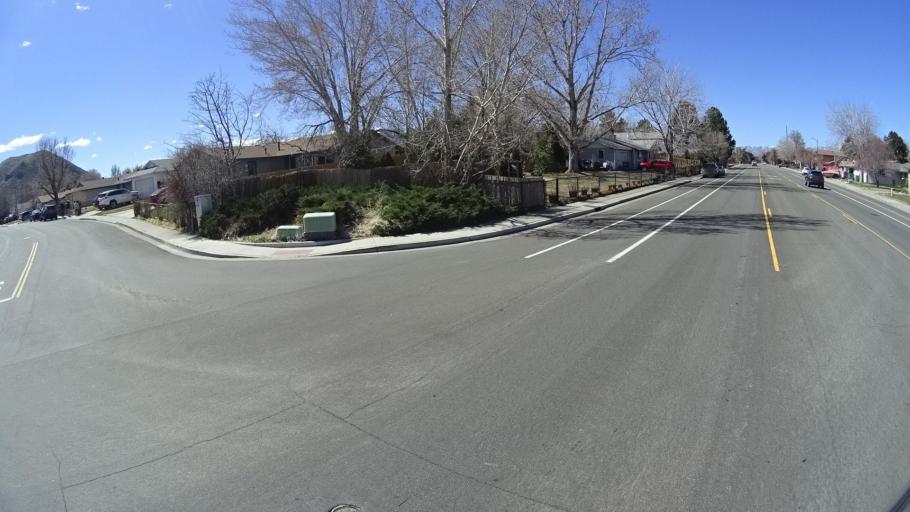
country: US
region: Nevada
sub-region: Washoe County
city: Sparks
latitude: 39.4861
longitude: -119.7556
